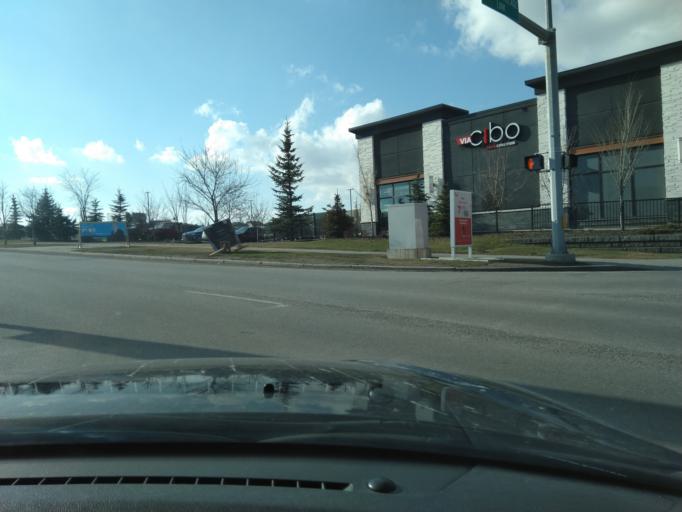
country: CA
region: Alberta
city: Calgary
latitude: 51.1604
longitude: -114.0679
